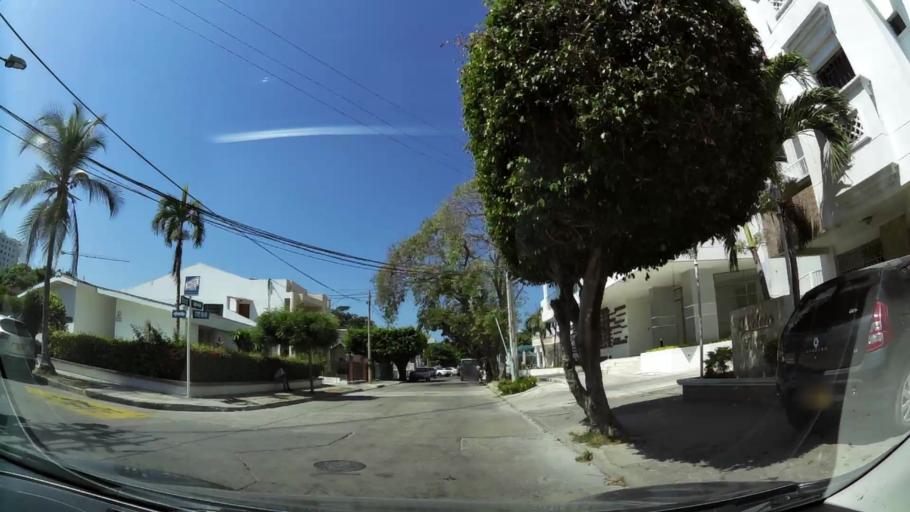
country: CO
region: Bolivar
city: Cartagena
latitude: 10.4465
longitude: -75.5180
